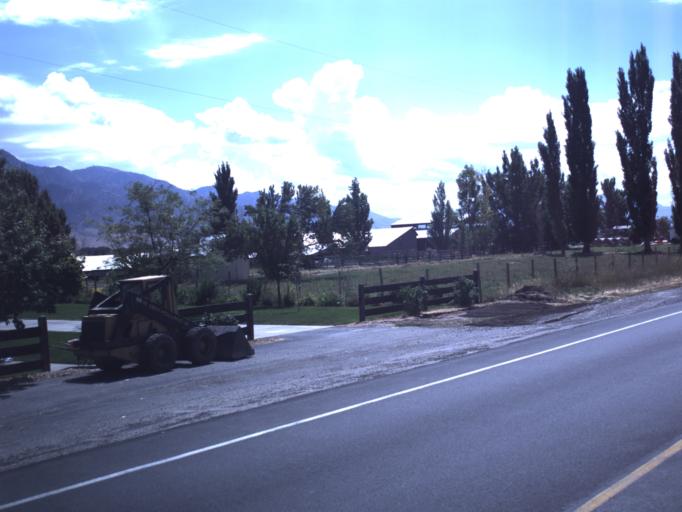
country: US
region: Utah
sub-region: Box Elder County
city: Elwood
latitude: 41.6870
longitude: -112.1415
